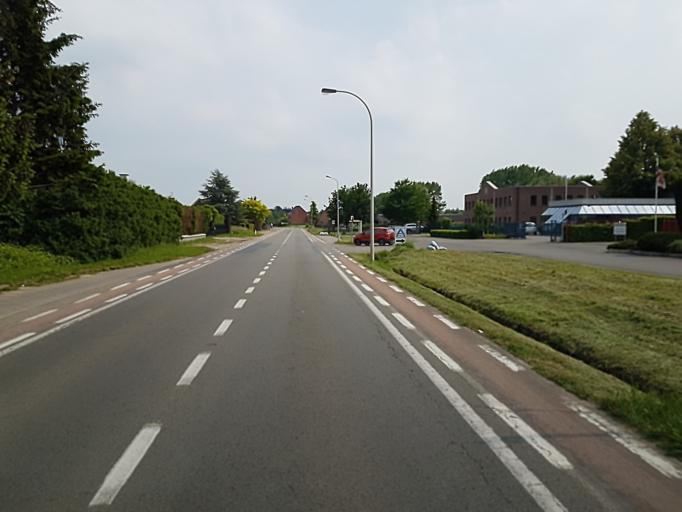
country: BE
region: Flanders
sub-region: Provincie Antwerpen
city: Ranst
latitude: 51.1929
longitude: 4.5524
